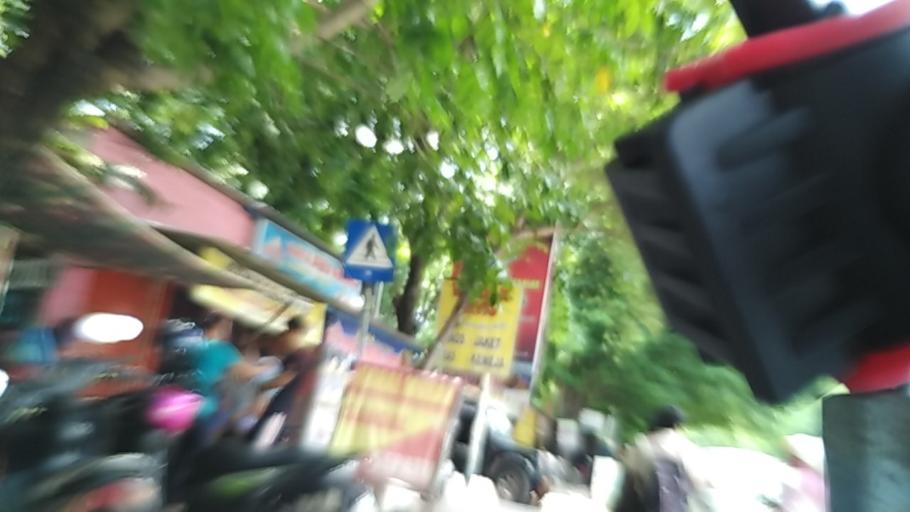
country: ID
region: Central Java
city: Semarang
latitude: -6.9903
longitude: 110.3853
